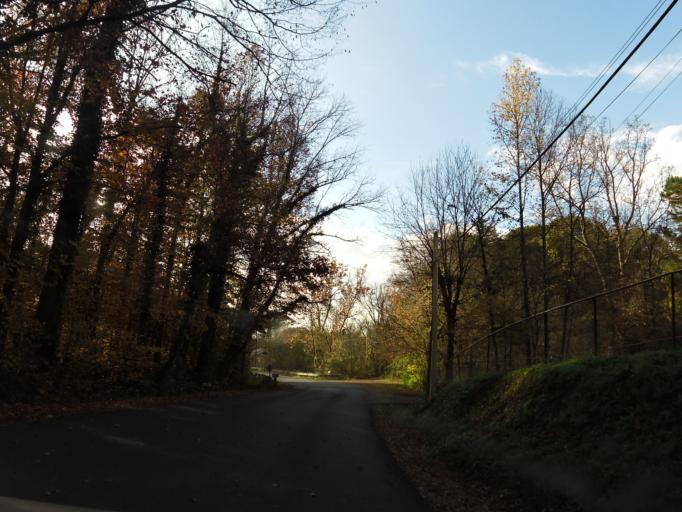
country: US
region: Tennessee
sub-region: Blount County
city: Eagleton Village
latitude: 35.8189
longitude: -83.9433
